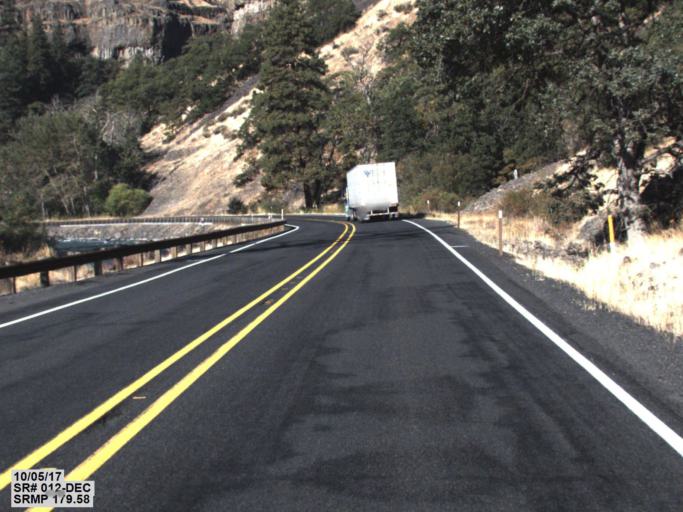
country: US
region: Washington
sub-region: Yakima County
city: Tieton
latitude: 46.7127
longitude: -120.8808
